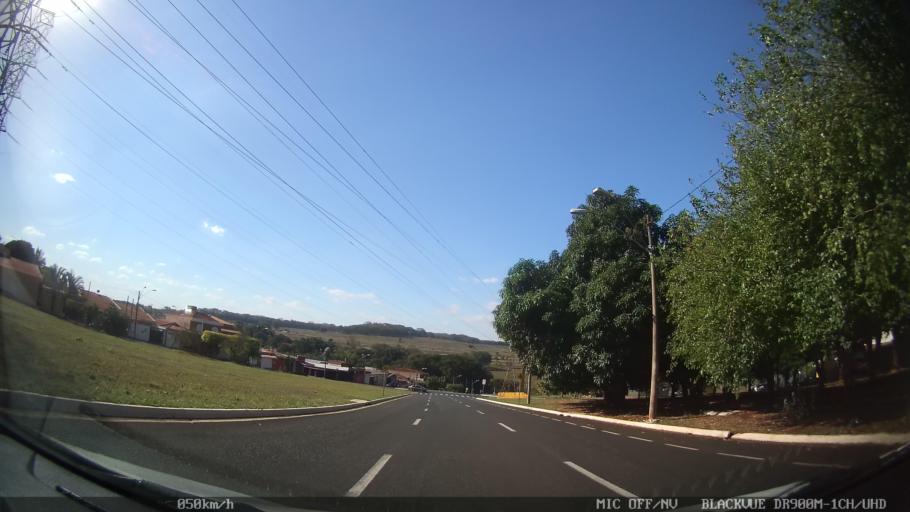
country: BR
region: Sao Paulo
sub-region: Ribeirao Preto
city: Ribeirao Preto
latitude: -21.1790
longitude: -47.7818
